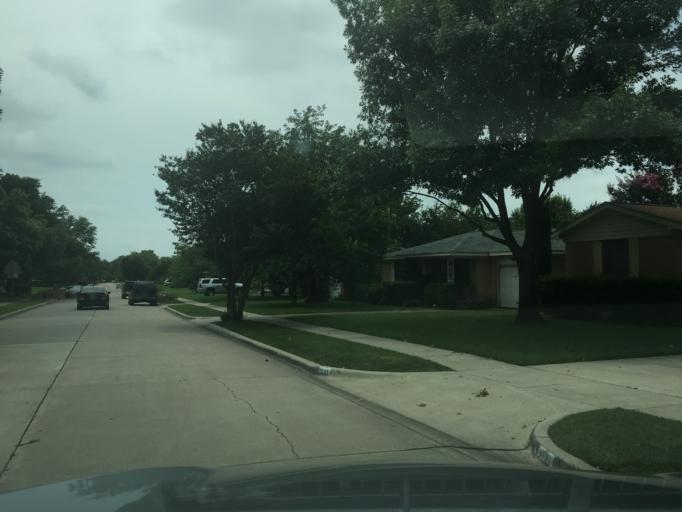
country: US
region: Texas
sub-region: Dallas County
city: Richardson
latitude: 32.9502
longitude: -96.7635
